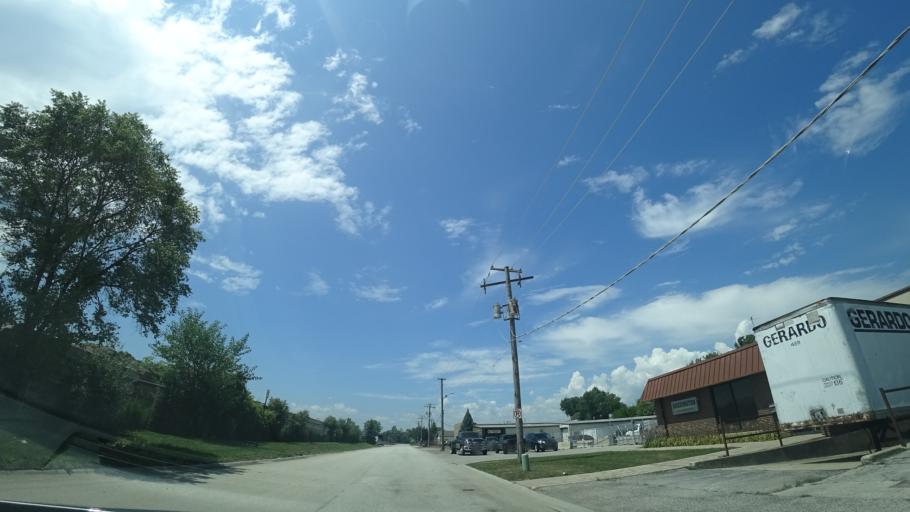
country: US
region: Illinois
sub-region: Cook County
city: Robbins
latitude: 41.6599
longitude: -87.7140
